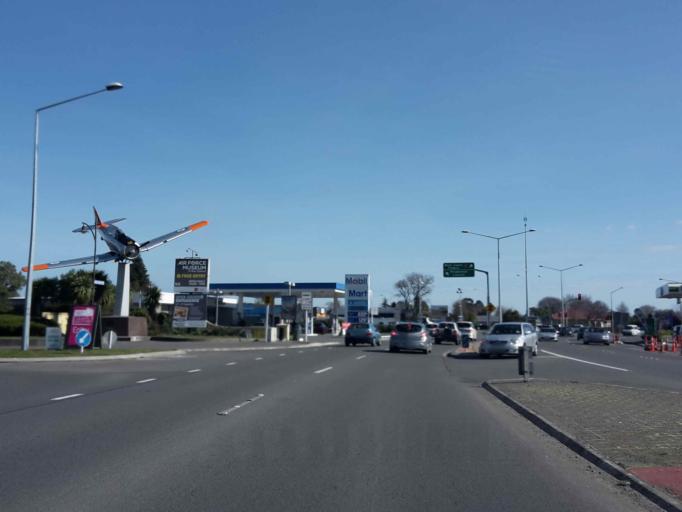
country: NZ
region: Canterbury
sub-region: Selwyn District
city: Prebbleton
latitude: -43.5428
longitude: 172.5473
